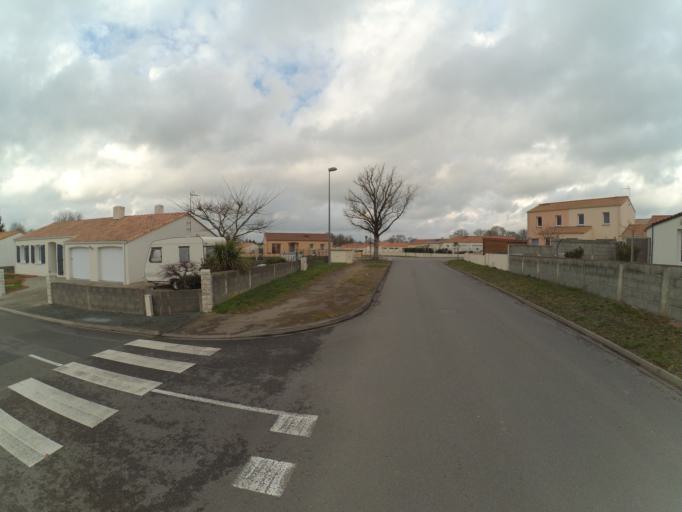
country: FR
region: Pays de la Loire
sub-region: Departement de la Vendee
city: Saint-Hilaire-de-Loulay
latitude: 47.0047
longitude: -1.3234
